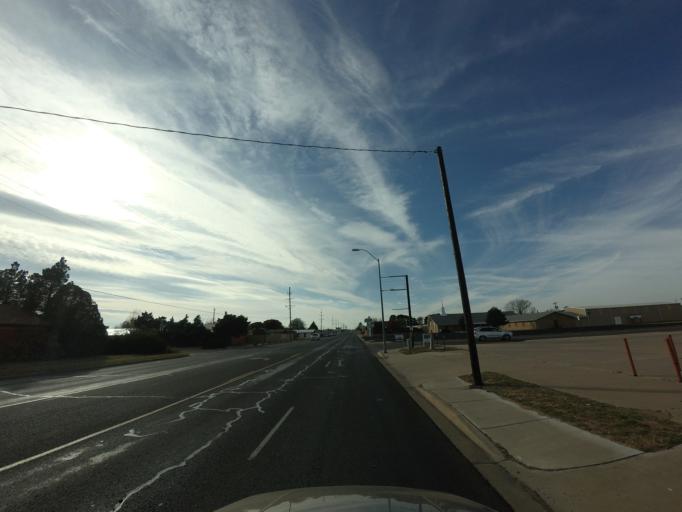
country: US
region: New Mexico
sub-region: Curry County
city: Clovis
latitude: 34.4194
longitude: -103.2206
